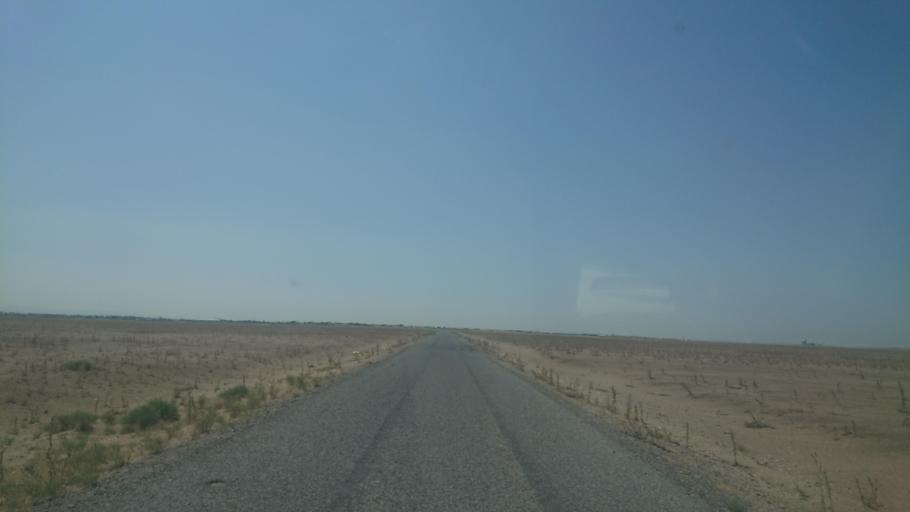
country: TR
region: Aksaray
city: Yesilova
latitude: 38.3088
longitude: 33.7361
